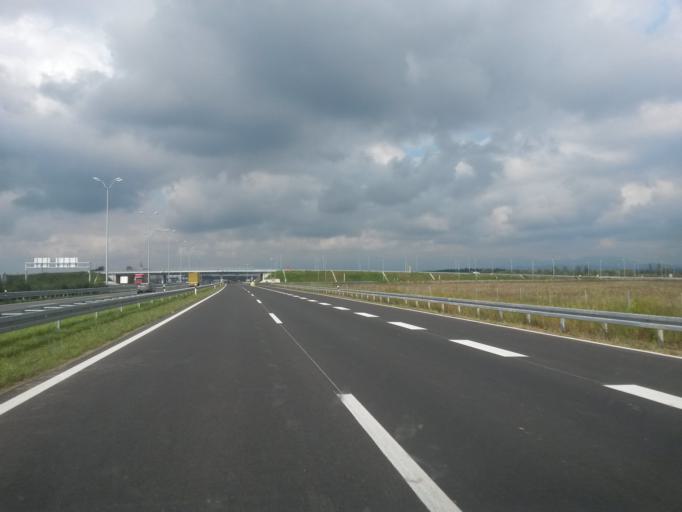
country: HR
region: Grad Zagreb
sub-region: Sesvete
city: Sesvete
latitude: 45.7911
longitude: 16.1686
